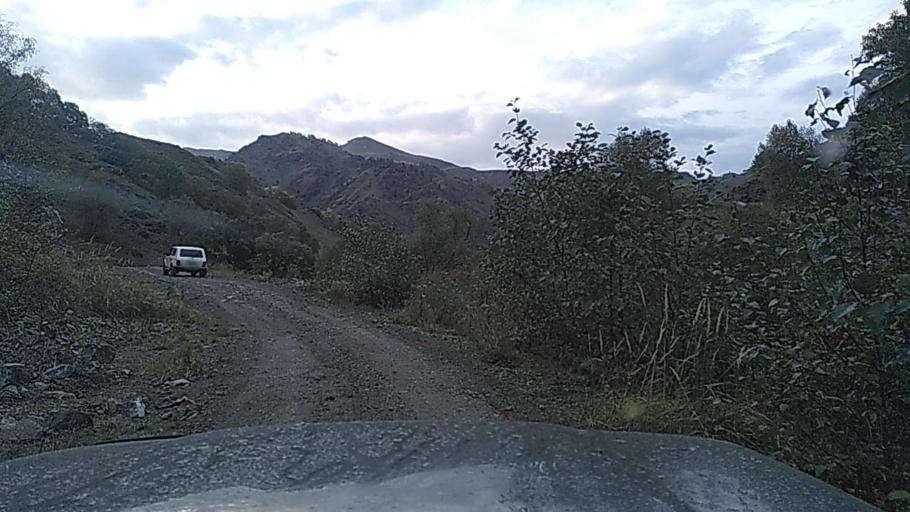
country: RU
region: Kabardino-Balkariya
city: Kamennomostskoye
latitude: 43.7145
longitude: 42.8467
